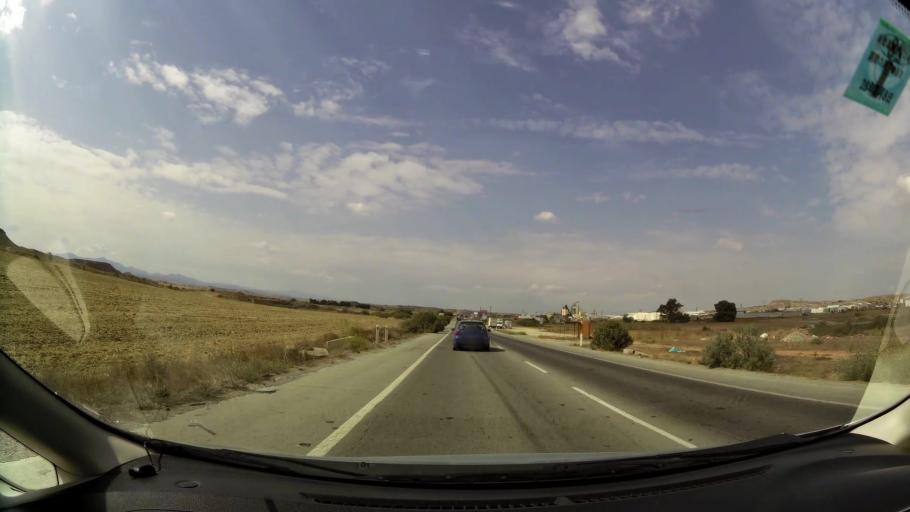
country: CY
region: Lefkosia
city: Tseri
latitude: 35.0592
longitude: 33.3598
